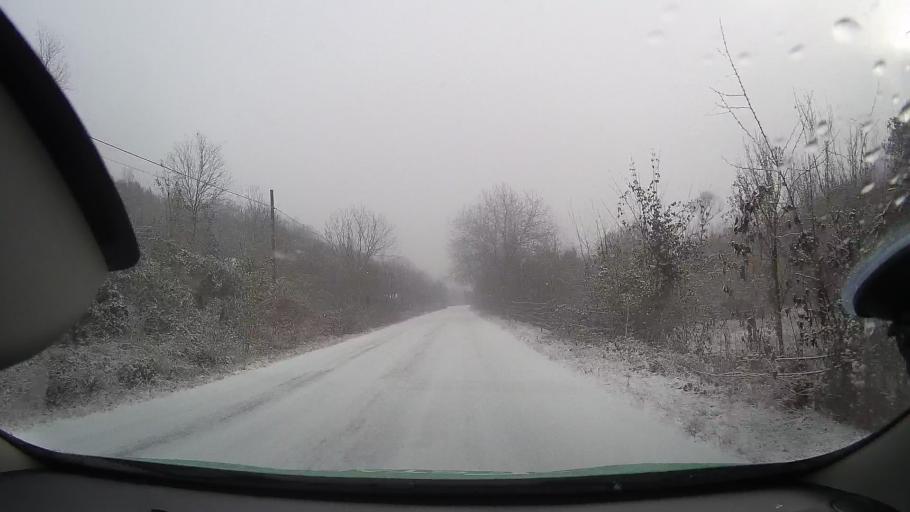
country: RO
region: Alba
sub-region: Comuna Livezile
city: Livezile
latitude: 46.3518
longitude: 23.6210
